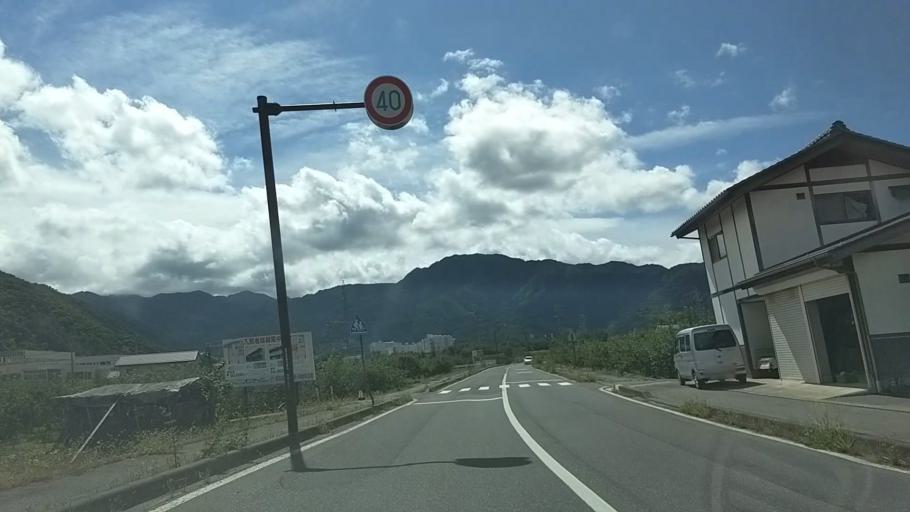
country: JP
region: Nagano
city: Suzaka
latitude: 36.6132
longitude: 138.2505
